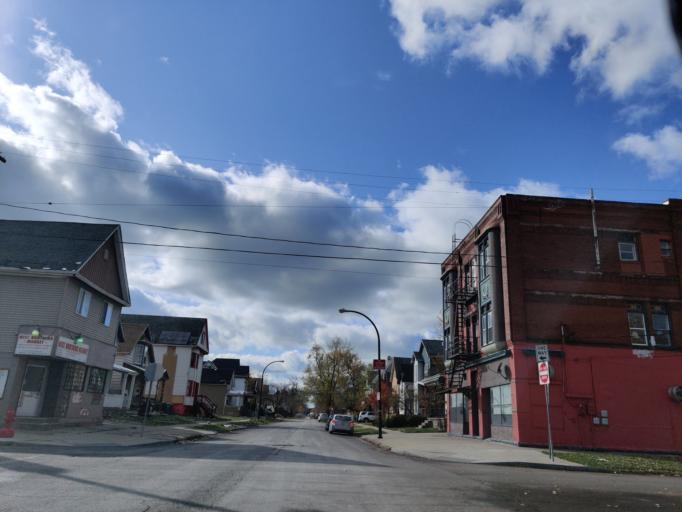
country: US
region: New York
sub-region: Erie County
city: Buffalo
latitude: 42.9106
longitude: -78.8922
